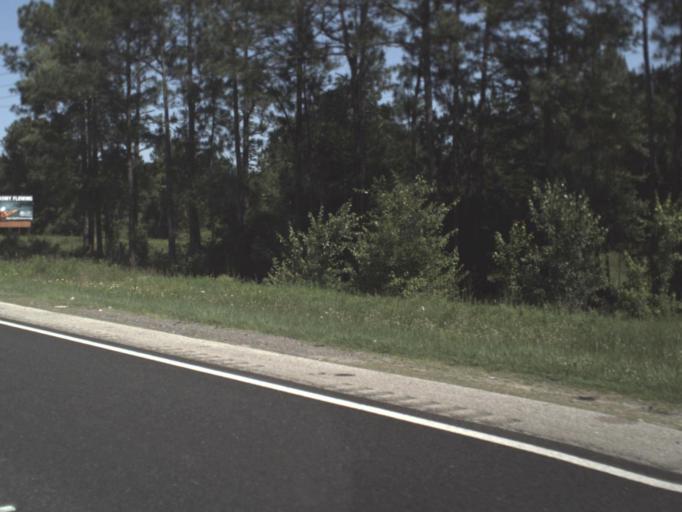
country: US
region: Florida
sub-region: Duval County
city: Baldwin
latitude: 30.2895
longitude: -81.9738
